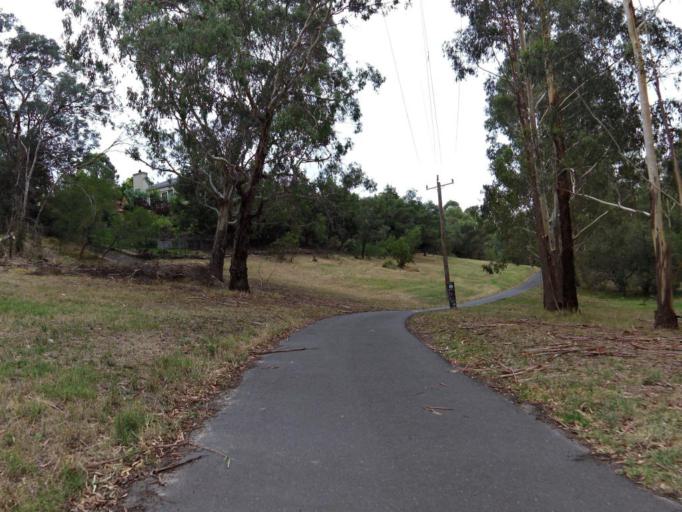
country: AU
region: Victoria
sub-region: Manningham
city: Templestowe Lower
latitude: -37.7620
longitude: 145.1271
